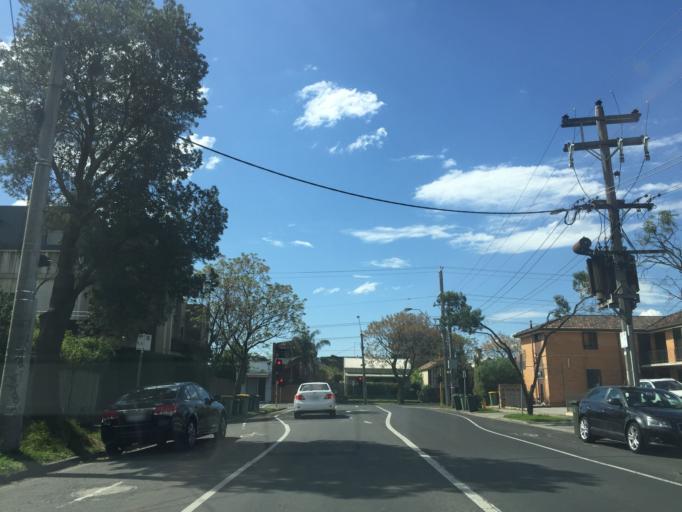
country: AU
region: Victoria
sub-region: Darebin
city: Fairfield
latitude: -37.7832
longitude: 145.0098
